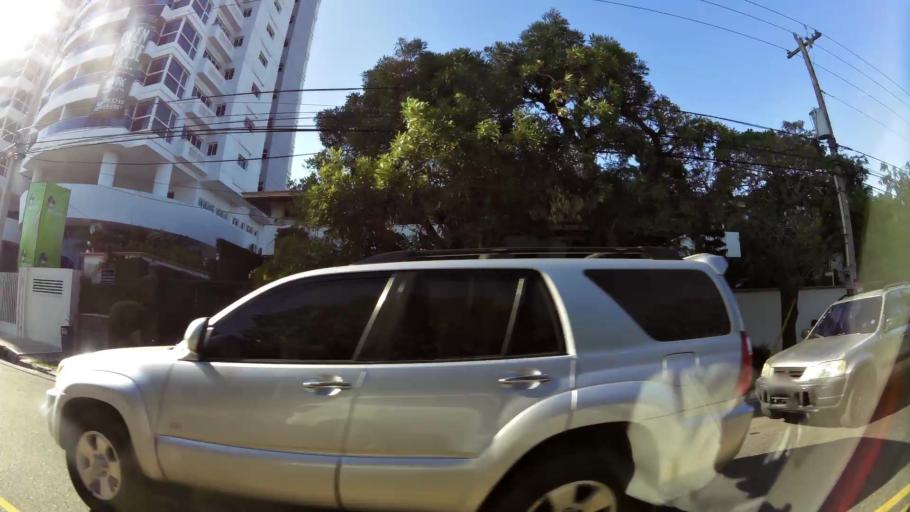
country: DO
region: Nacional
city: Bella Vista
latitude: 18.4418
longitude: -69.9614
